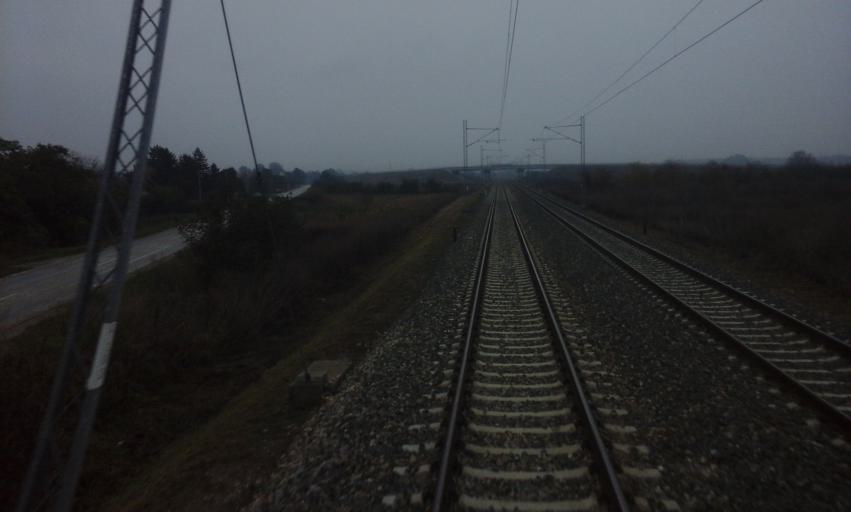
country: RS
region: Central Serbia
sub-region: Pomoravski Okrug
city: Cuprija
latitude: 43.9508
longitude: 21.3243
